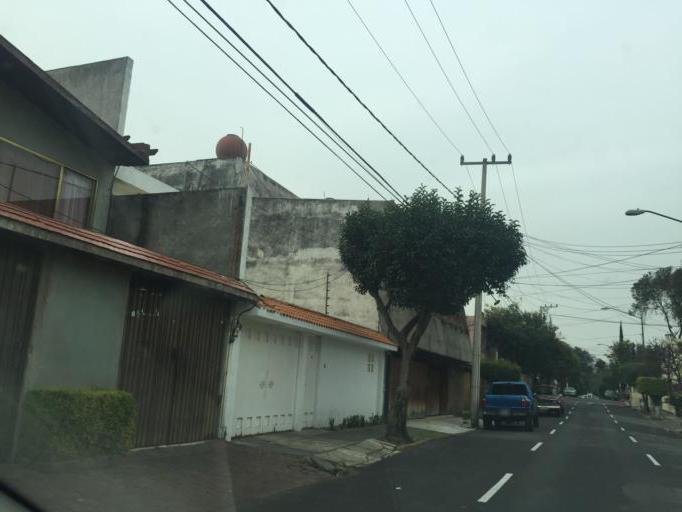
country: MX
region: Mexico
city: Colonia Lindavista
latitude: 19.4952
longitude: -99.1243
